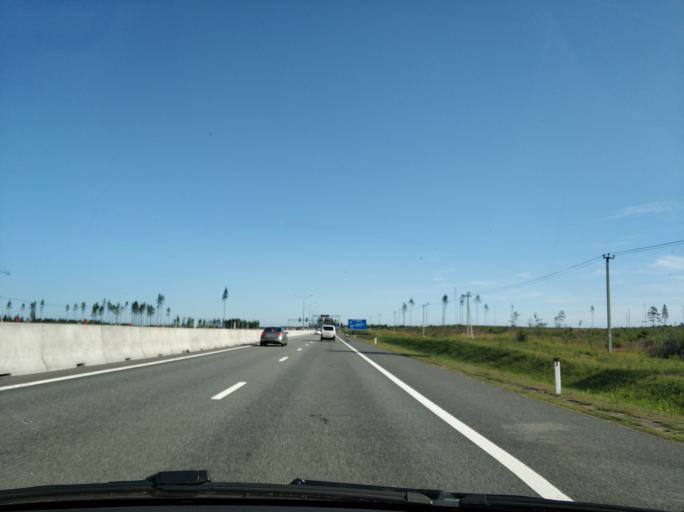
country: RU
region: Leningrad
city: Sosnovo
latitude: 60.4952
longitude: 30.1958
